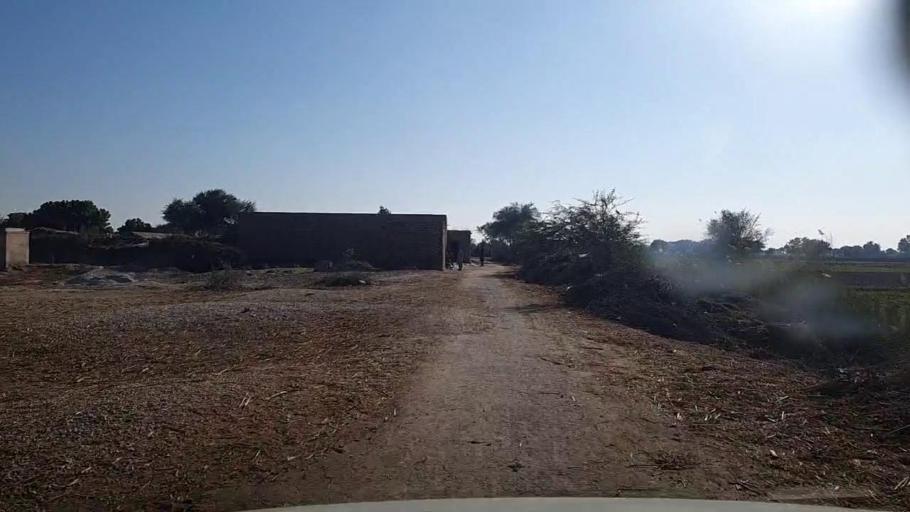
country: PK
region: Sindh
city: Khairpur
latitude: 27.9804
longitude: 69.7683
